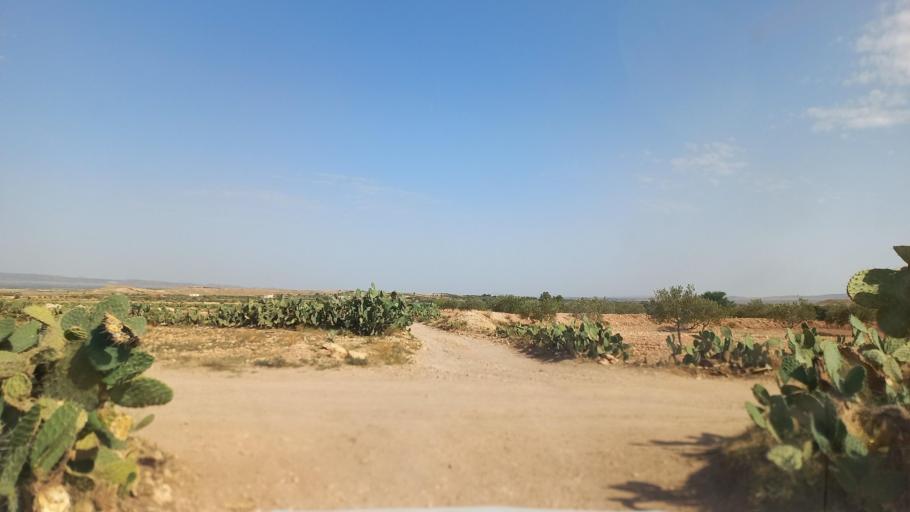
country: TN
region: Al Qasrayn
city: Kasserine
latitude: 35.2826
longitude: 8.9491
